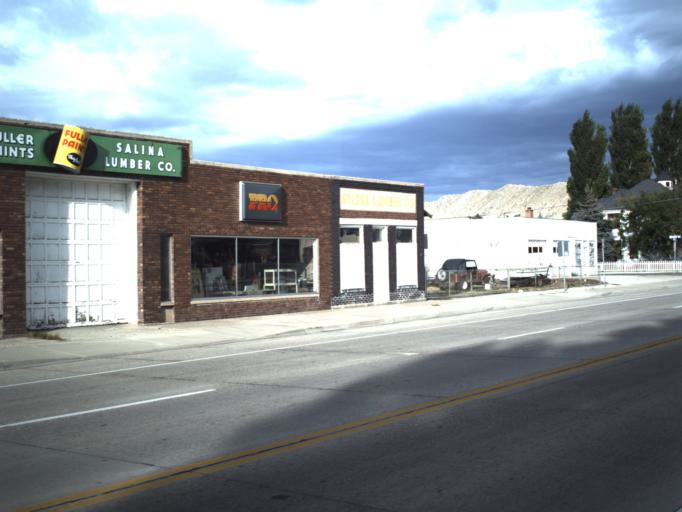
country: US
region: Utah
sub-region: Sevier County
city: Salina
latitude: 38.9577
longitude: -111.8645
